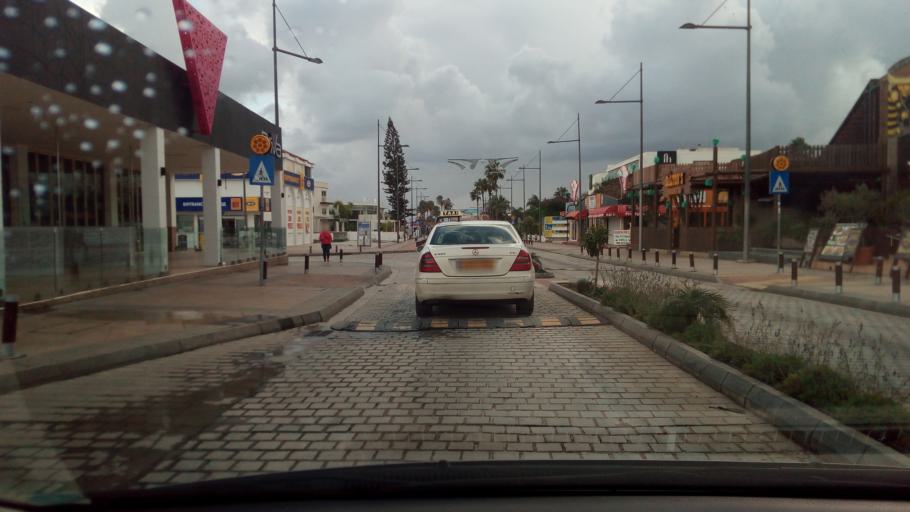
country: CY
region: Ammochostos
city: Ayia Napa
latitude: 34.9850
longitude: 34.0005
